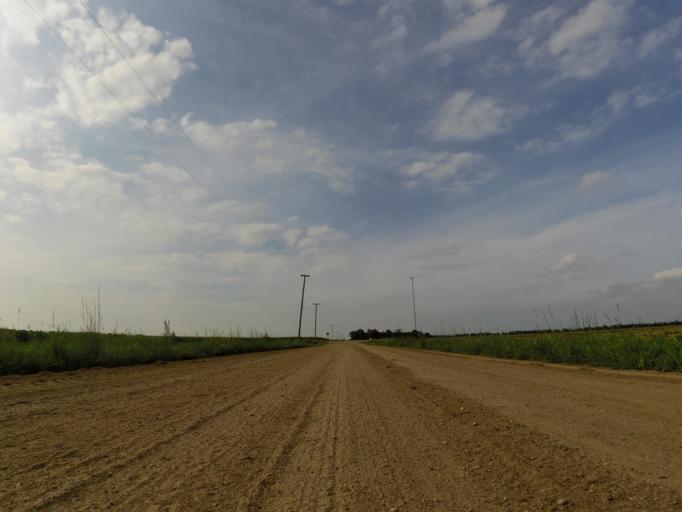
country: US
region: Kansas
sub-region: Reno County
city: South Hutchinson
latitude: 37.9691
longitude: -98.0688
